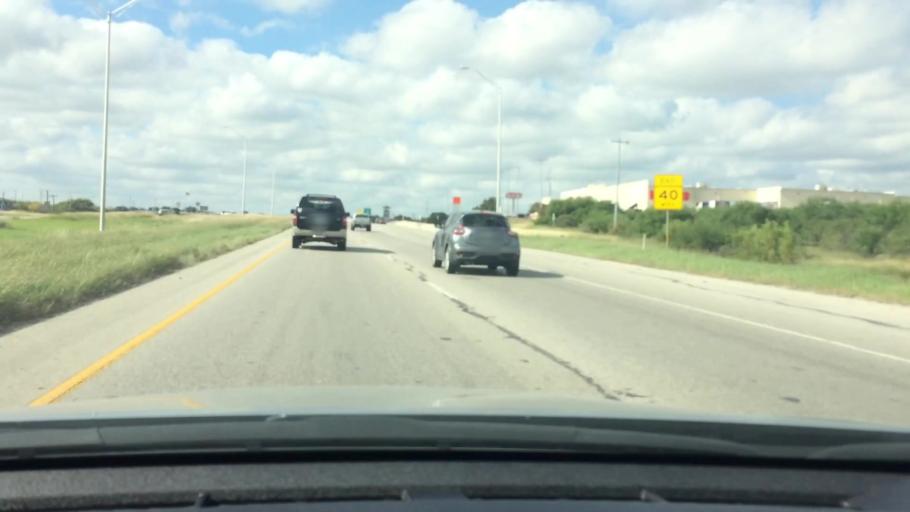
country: US
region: Texas
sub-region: Bexar County
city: Universal City
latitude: 29.5438
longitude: -98.3104
